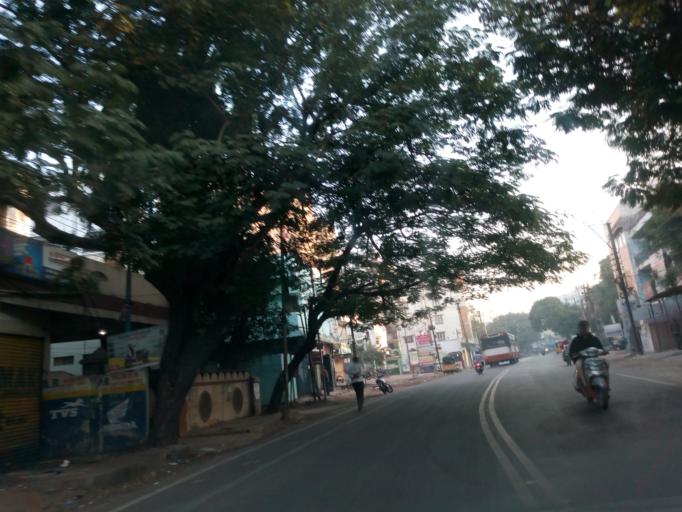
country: IN
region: Telangana
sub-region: Rangareddi
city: Gaddi Annaram
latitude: 17.4052
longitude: 78.5110
